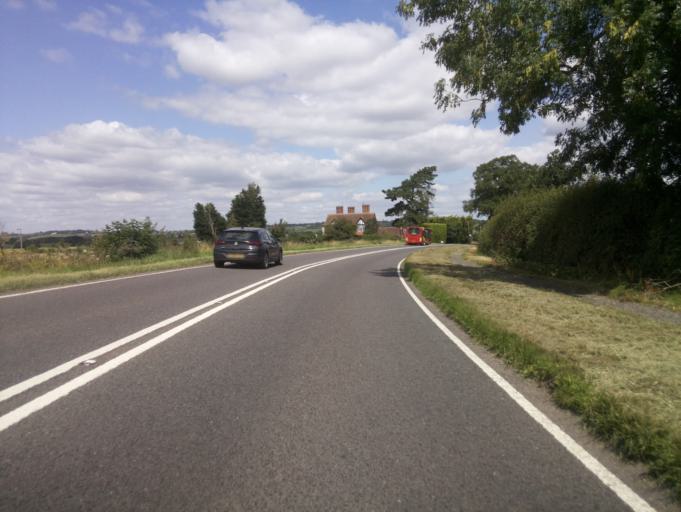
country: GB
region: England
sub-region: Buckinghamshire
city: Aylesbury
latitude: 51.8568
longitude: -0.8299
